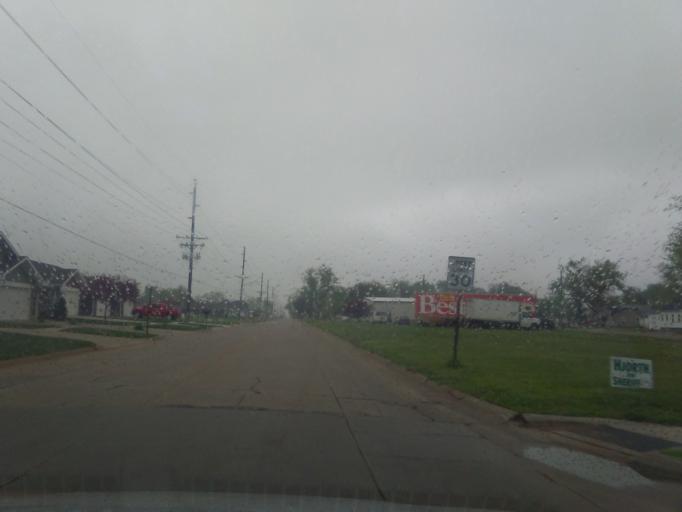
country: US
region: Nebraska
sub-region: Madison County
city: Norfolk
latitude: 42.0401
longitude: -97.4183
